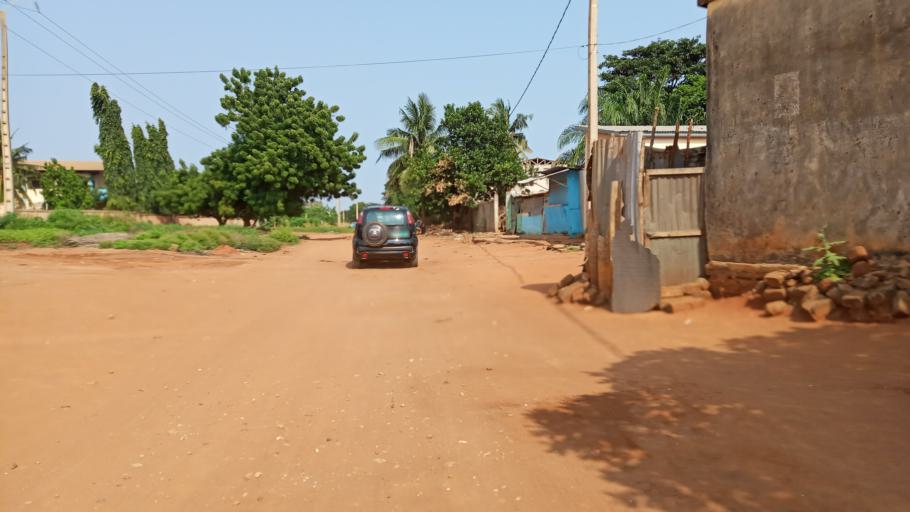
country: TG
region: Maritime
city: Lome
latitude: 6.2095
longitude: 1.1994
